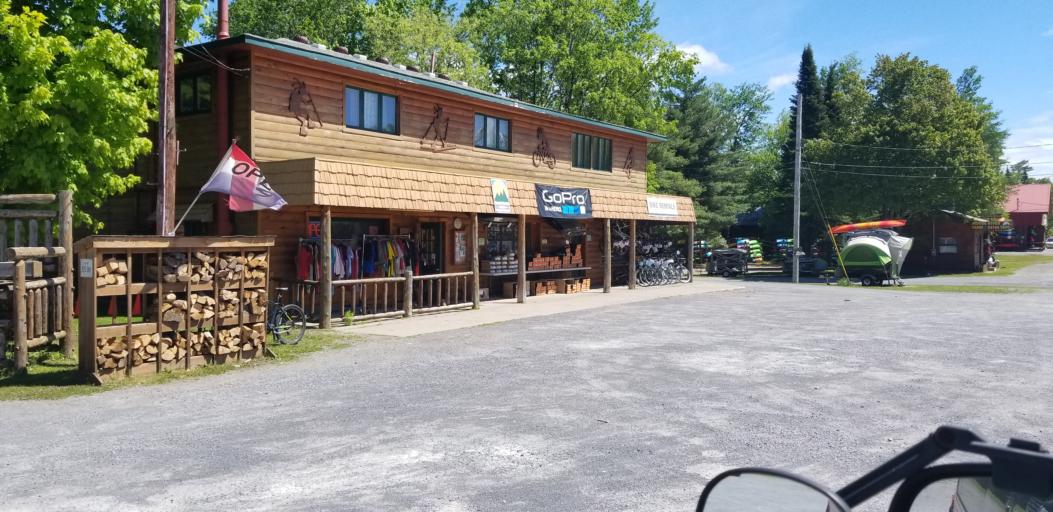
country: US
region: New York
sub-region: Oneida County
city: Boonville
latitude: 43.7030
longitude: -74.9878
